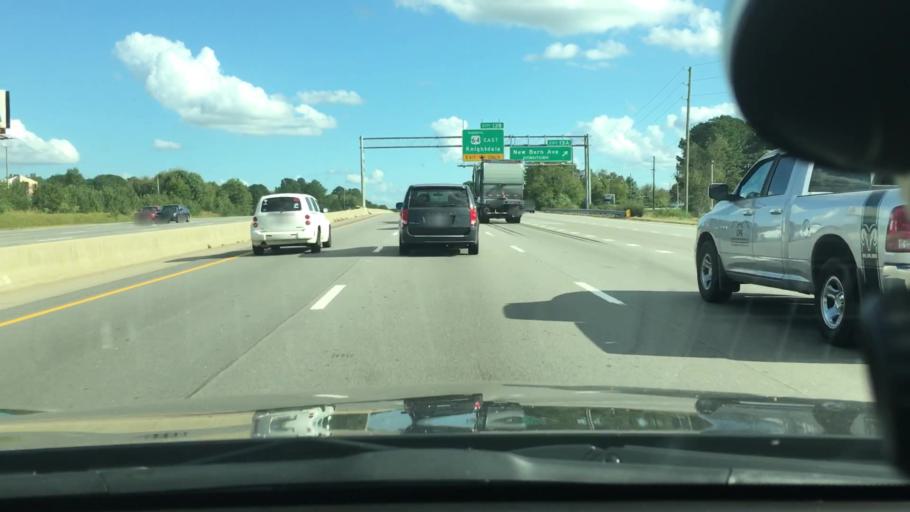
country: US
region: North Carolina
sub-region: Wake County
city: Raleigh
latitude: 35.7973
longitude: -78.5868
